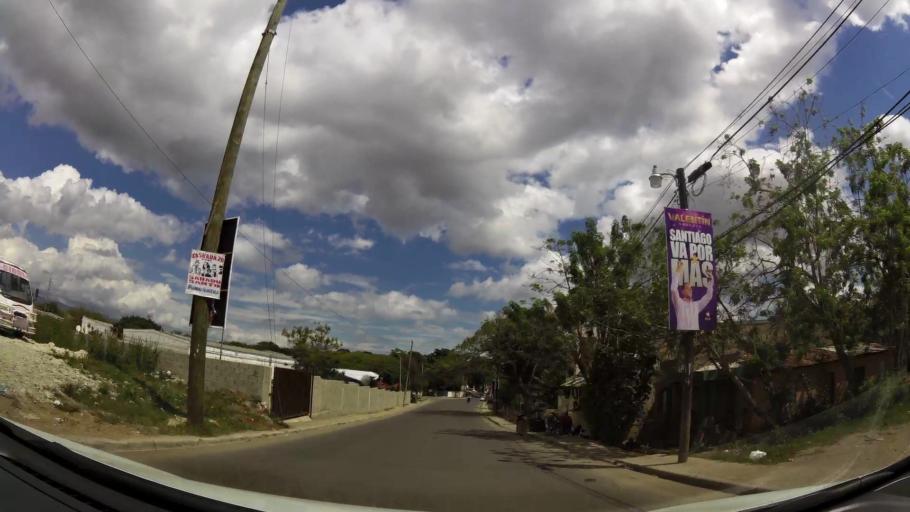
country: DO
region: Santiago
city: Santiago de los Caballeros
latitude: 19.4065
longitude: -70.6654
